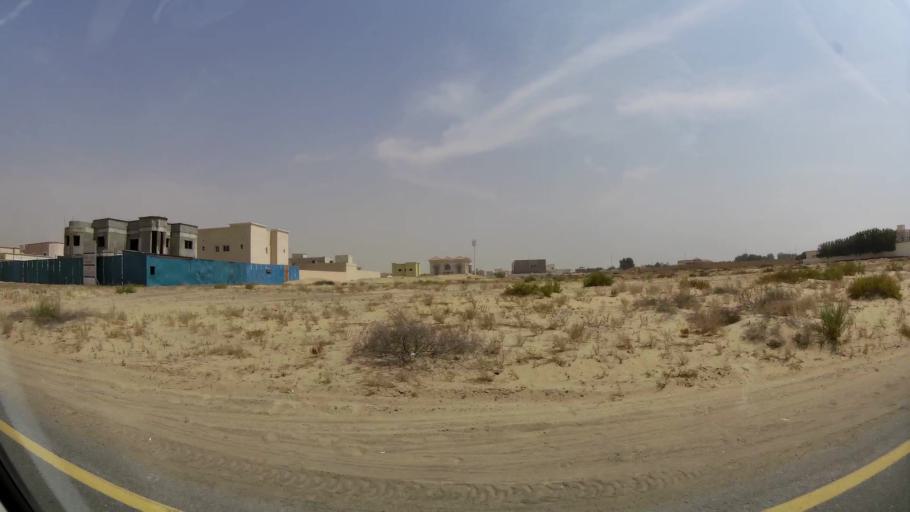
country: AE
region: Ash Shariqah
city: Sharjah
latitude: 25.2510
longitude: 55.4729
